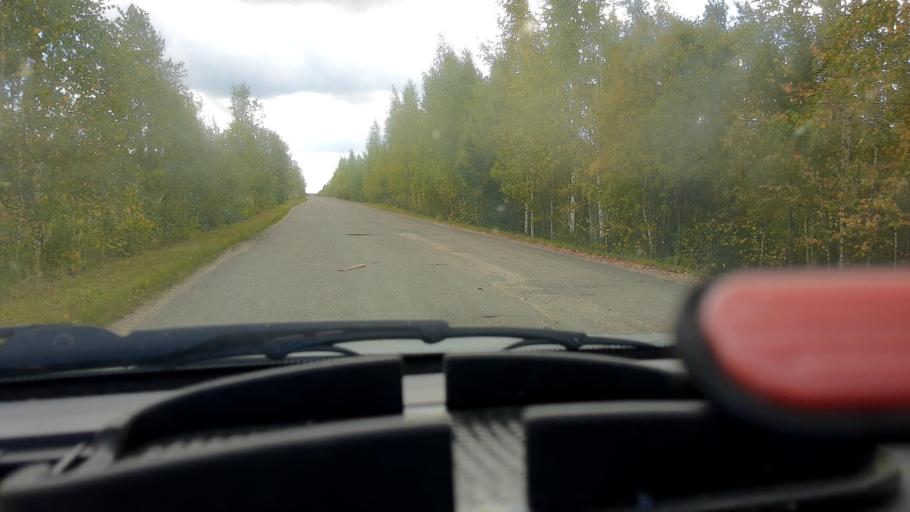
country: RU
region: Mariy-El
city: Kilemary
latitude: 56.9005
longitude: 46.7432
